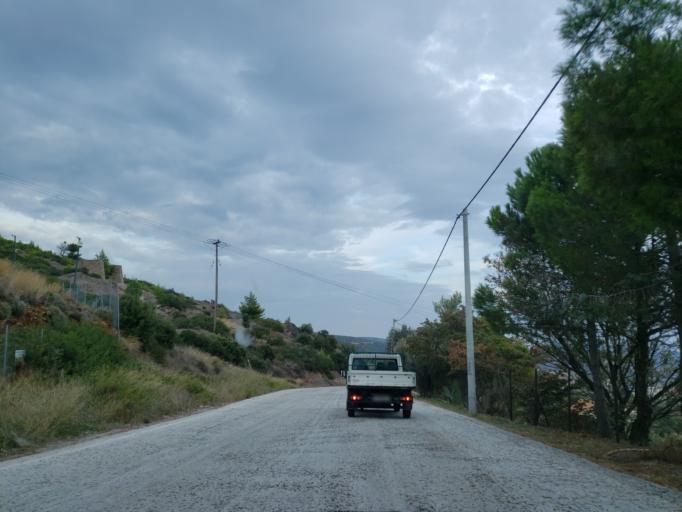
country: GR
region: Attica
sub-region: Nomarchia Anatolikis Attikis
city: Grammatiko
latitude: 38.2048
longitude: 23.9567
